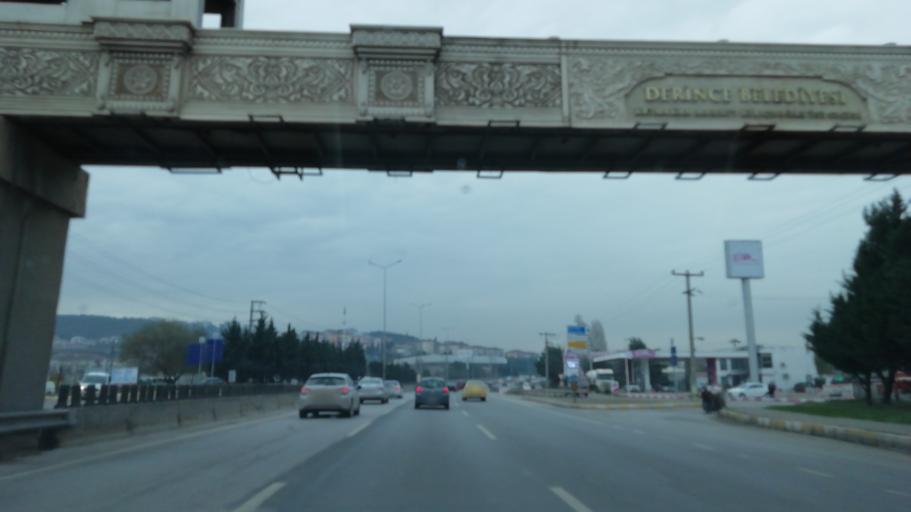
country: TR
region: Kocaeli
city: Derince
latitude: 40.7611
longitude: 29.8517
